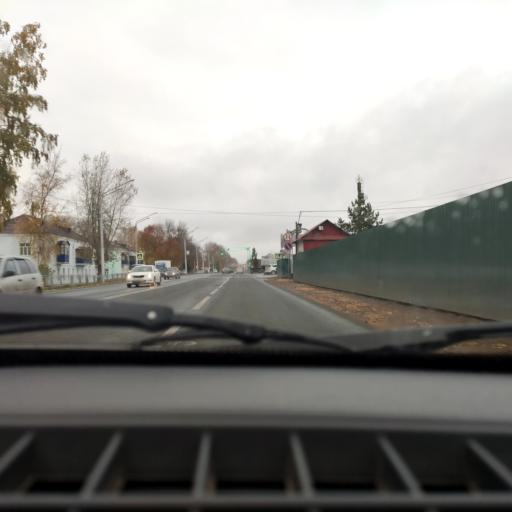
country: RU
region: Bashkortostan
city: Avdon
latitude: 54.6959
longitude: 55.8290
